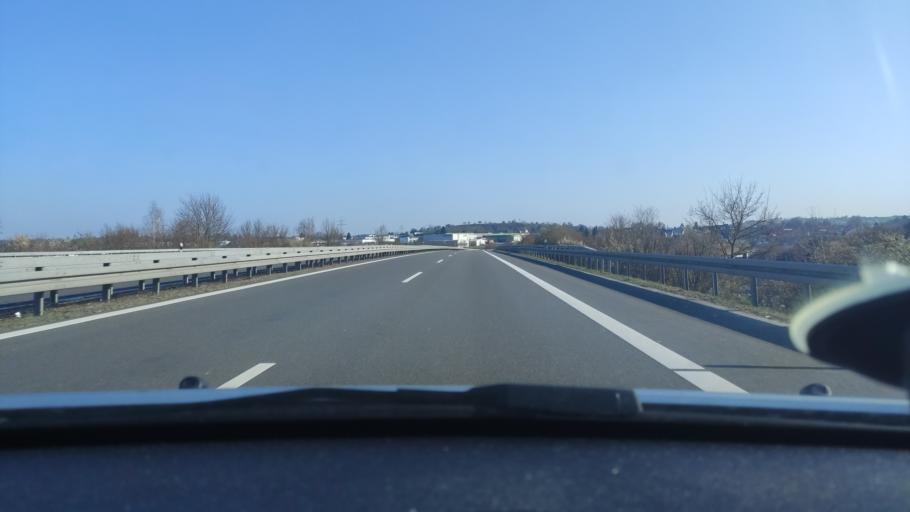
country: DE
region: Baden-Wuerttemberg
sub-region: Tuebingen Region
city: Balingen
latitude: 48.2926
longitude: 8.8653
